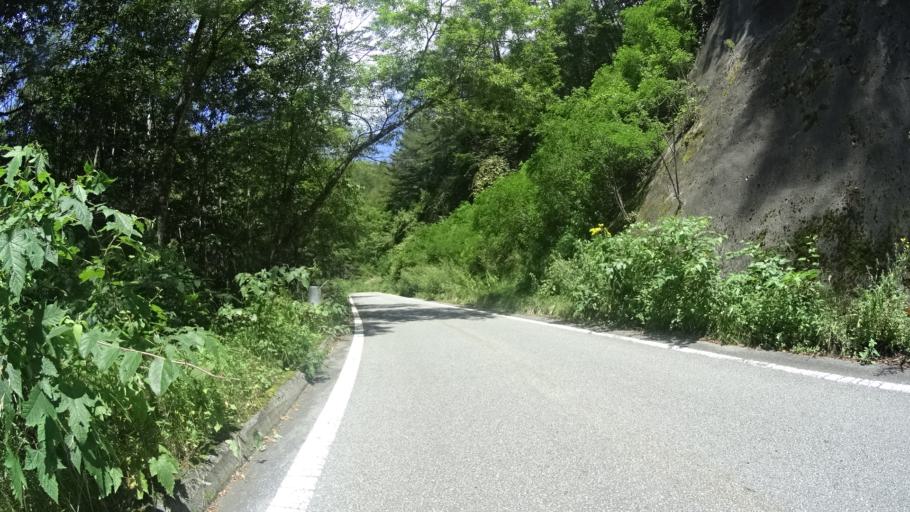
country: JP
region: Yamanashi
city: Enzan
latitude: 35.8213
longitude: 138.6545
